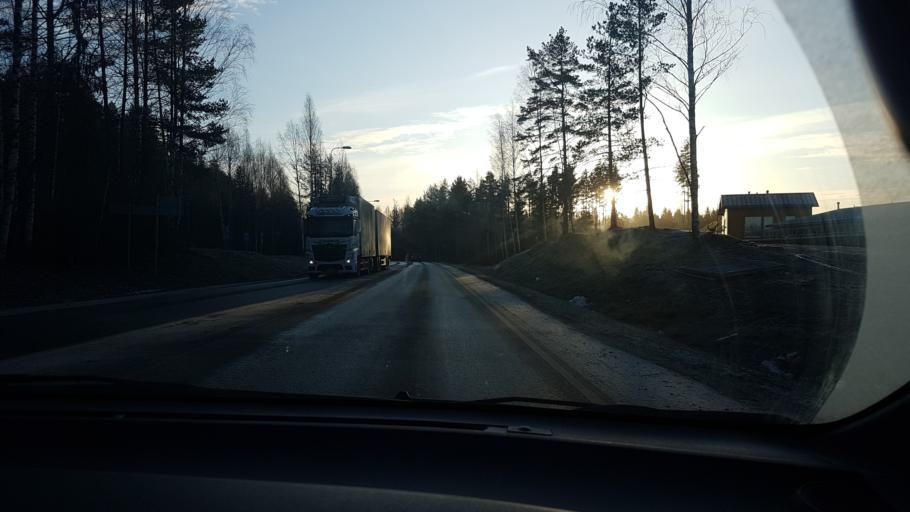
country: FI
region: Uusimaa
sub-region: Helsinki
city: Tuusula
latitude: 60.3980
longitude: 25.0525
